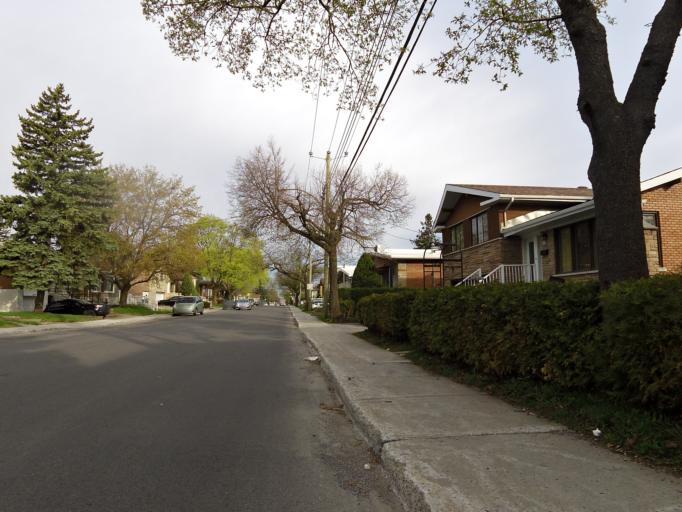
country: CA
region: Quebec
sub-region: Laval
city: Laval
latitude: 45.5385
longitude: -73.6803
